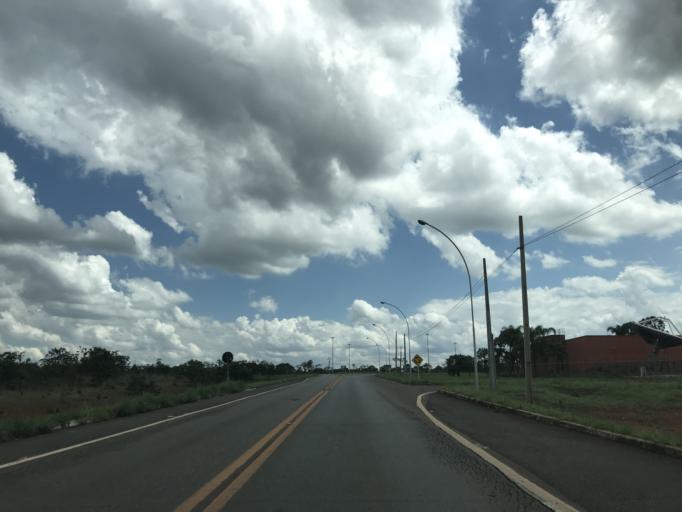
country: BR
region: Federal District
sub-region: Brasilia
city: Brasilia
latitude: -15.6917
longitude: -47.8345
